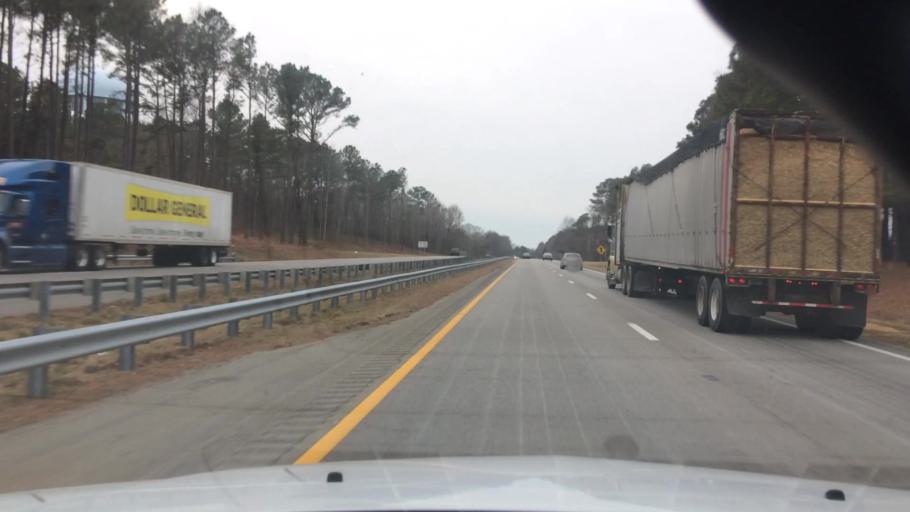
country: US
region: North Carolina
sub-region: Nash County
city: Red Oak
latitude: 35.9811
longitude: -77.8979
